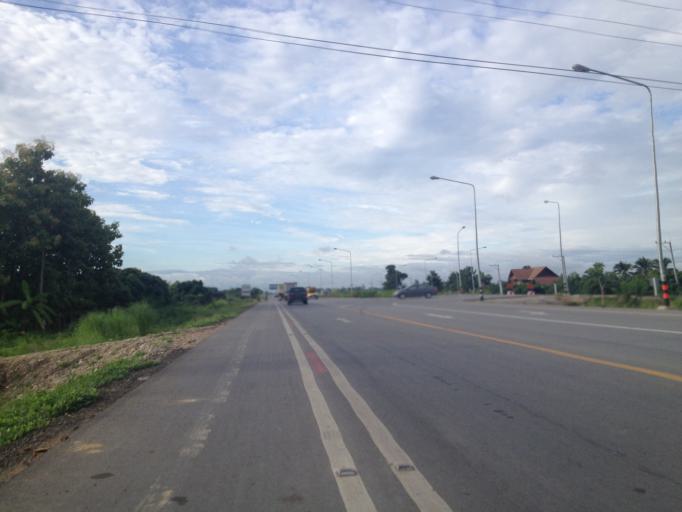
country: TH
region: Chiang Mai
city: San Pa Tong
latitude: 18.6355
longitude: 98.8404
